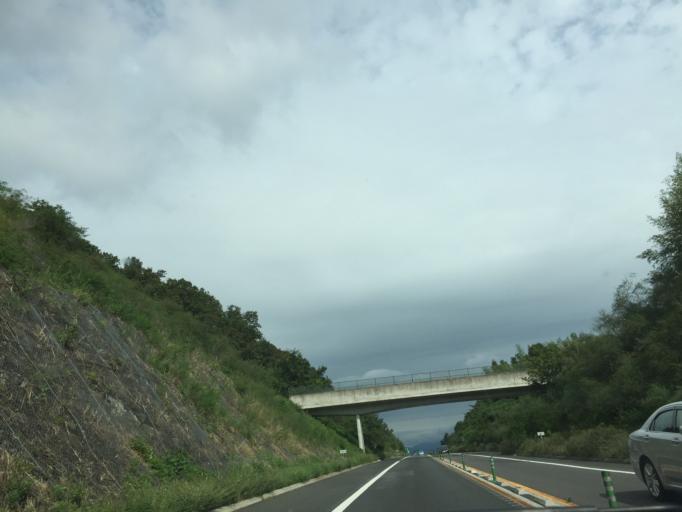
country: JP
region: Kagawa
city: Shido
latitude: 34.2642
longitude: 134.2869
